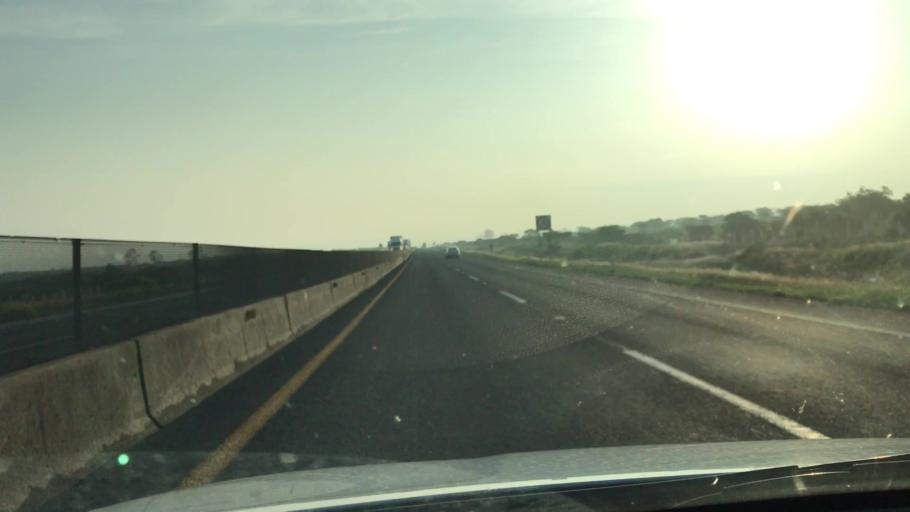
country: MX
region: Jalisco
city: Jalostotitlan
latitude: 21.0646
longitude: -102.5143
